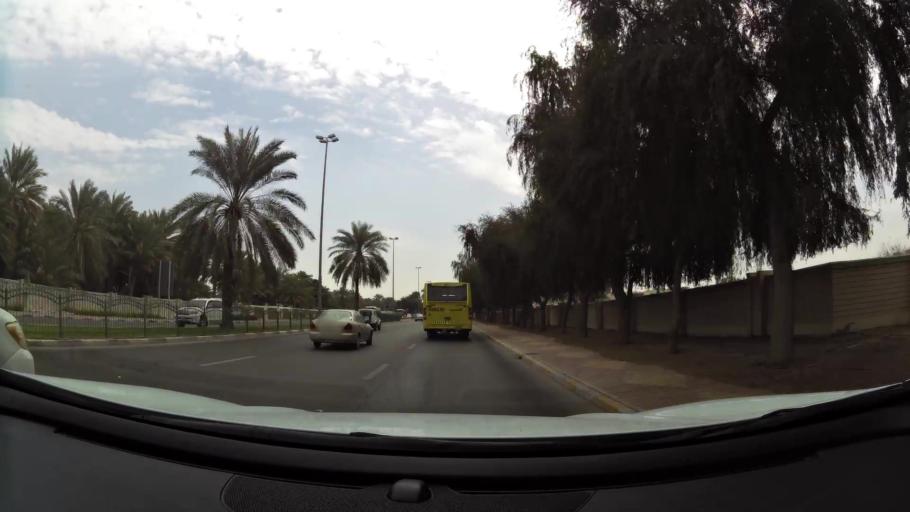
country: OM
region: Al Buraimi
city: Al Buraymi
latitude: 24.2225
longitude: 55.7850
